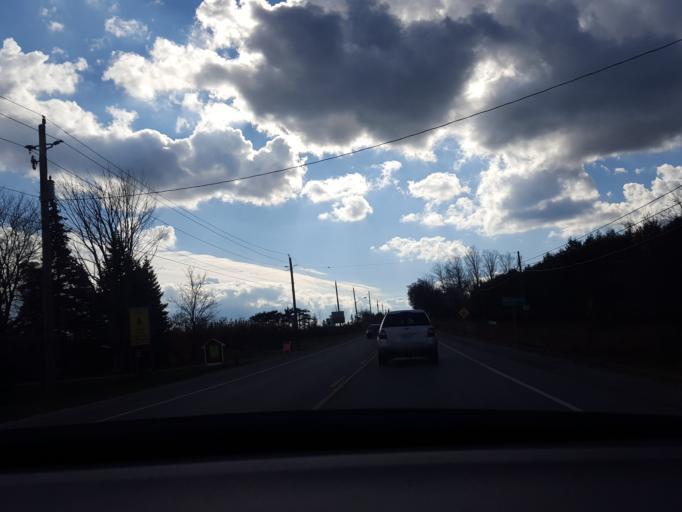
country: CA
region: Ontario
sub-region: Halton
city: Milton
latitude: 43.4780
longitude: -79.8932
